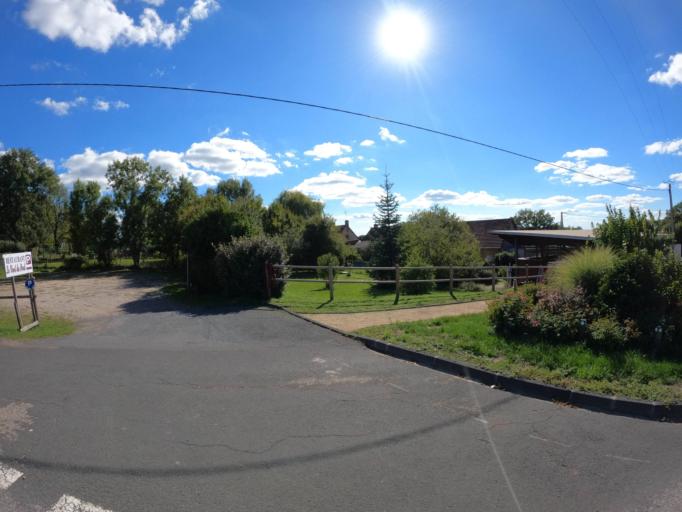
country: FR
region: Auvergne
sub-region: Departement de l'Allier
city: Buxieres-les-Mines
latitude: 46.4054
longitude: 2.9111
